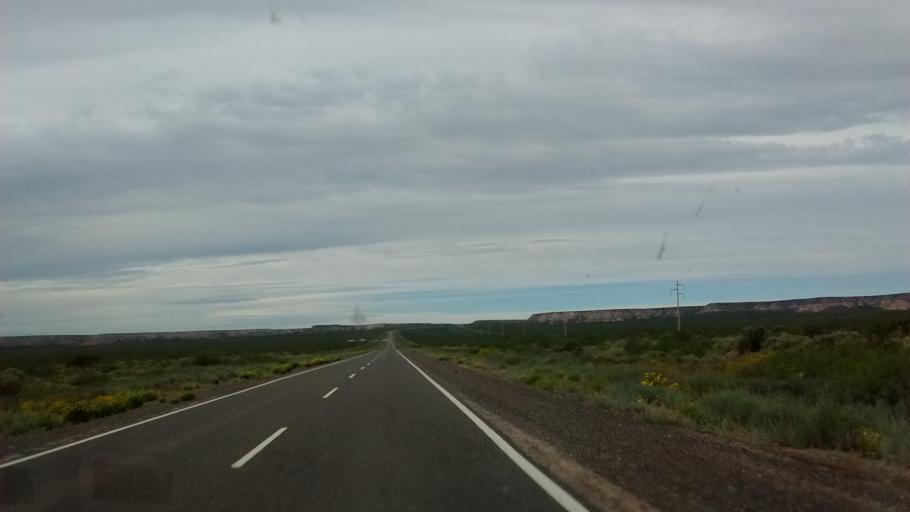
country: AR
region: Rio Negro
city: Catriel
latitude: -38.1637
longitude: -67.9492
